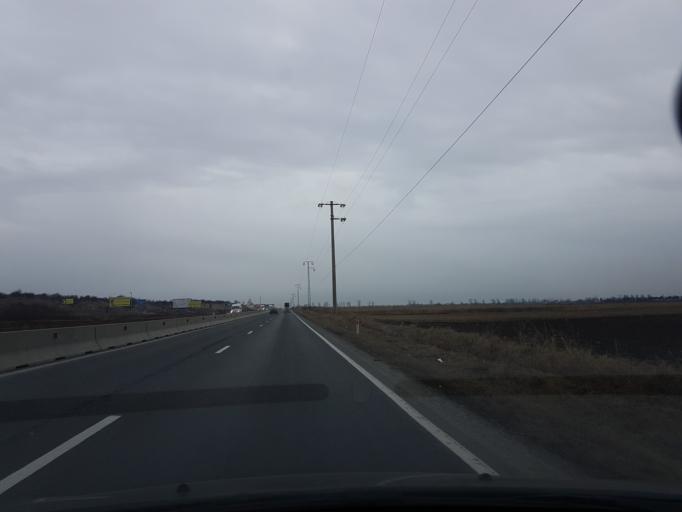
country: RO
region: Prahova
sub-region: Comuna Floresti
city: Floresti
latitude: 45.0576
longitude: 25.7972
